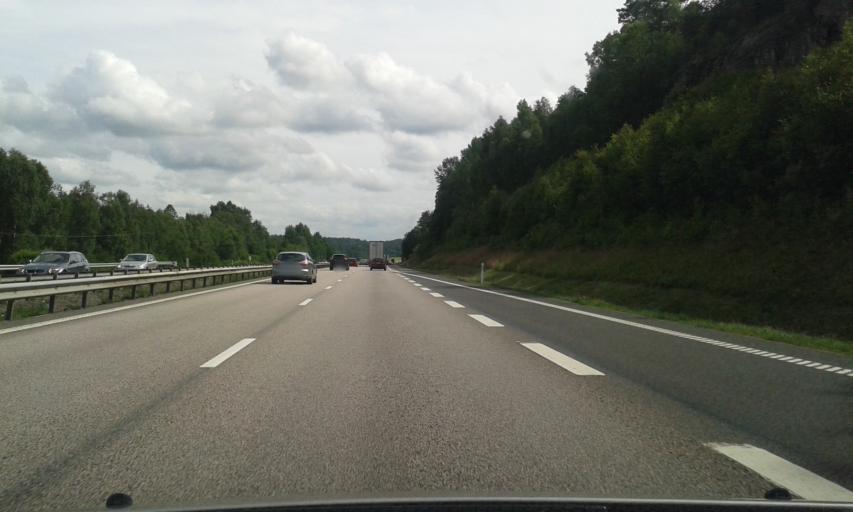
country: SE
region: Halland
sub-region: Kungsbacka Kommun
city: Frillesas
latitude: 57.3792
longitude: 12.1959
